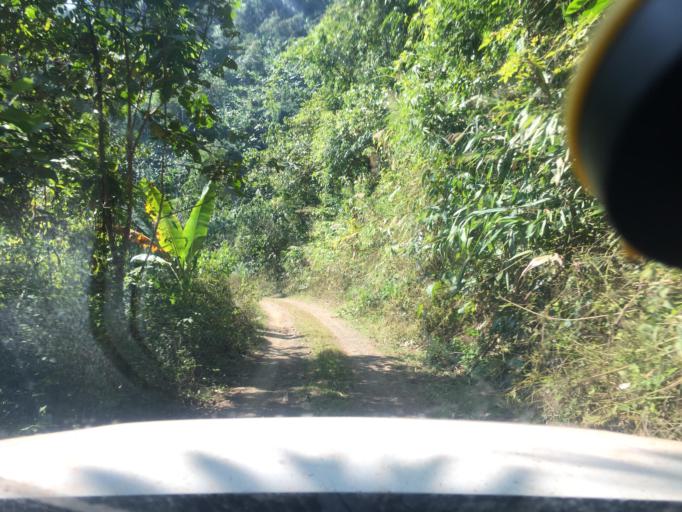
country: LA
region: Phongsali
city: Phongsali
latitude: 21.6855
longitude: 102.4076
